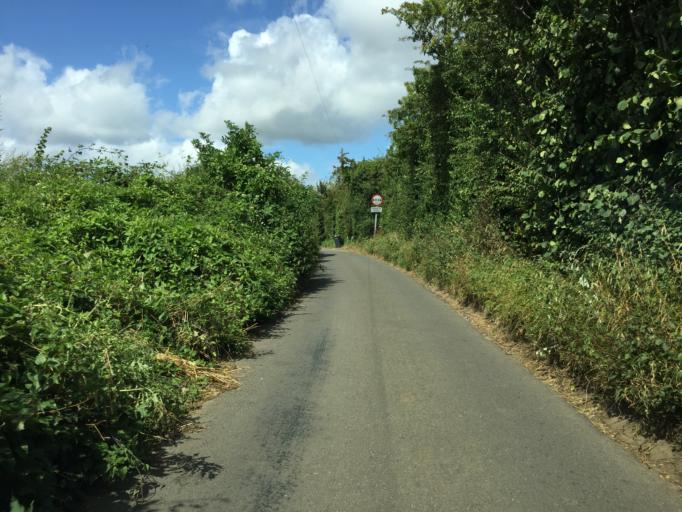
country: GB
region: England
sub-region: Kent
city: West Malling
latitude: 51.2981
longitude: 0.3960
